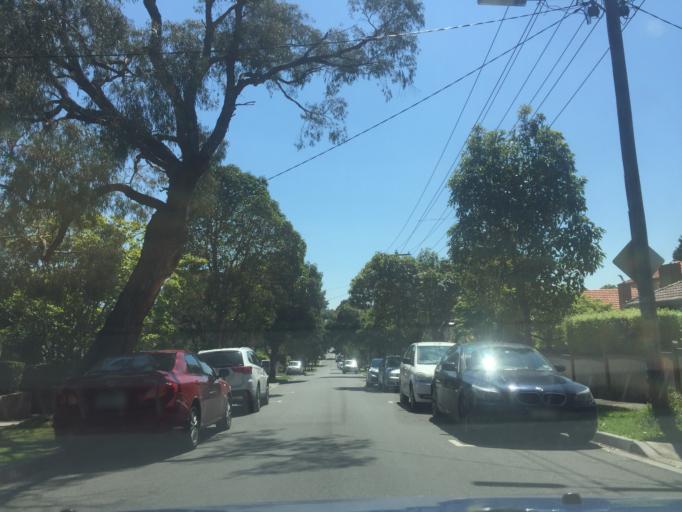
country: AU
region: Victoria
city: Mont Albert
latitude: -37.8166
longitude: 145.0923
